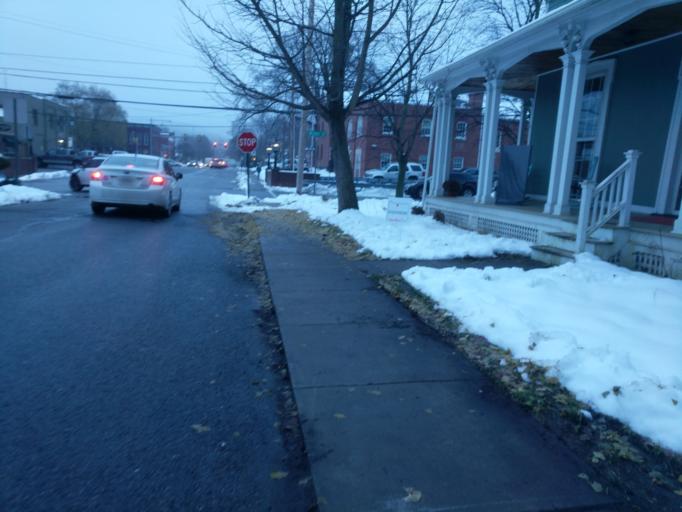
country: US
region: Pennsylvania
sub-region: Tioga County
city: Wellsboro
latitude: 41.7483
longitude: -77.3031
